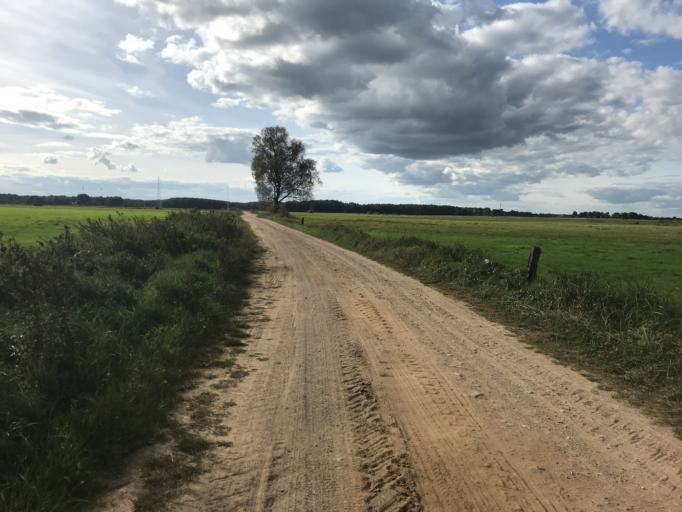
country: PL
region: Podlasie
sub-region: Powiat zambrowski
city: Rutki
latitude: 53.2022
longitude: 22.5829
